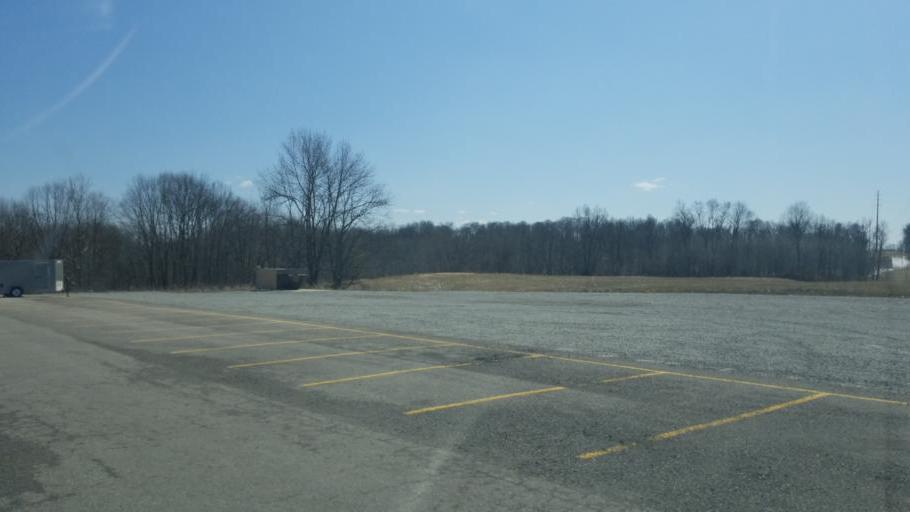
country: US
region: Ohio
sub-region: Highland County
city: Hillsboro
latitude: 39.1815
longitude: -83.6179
